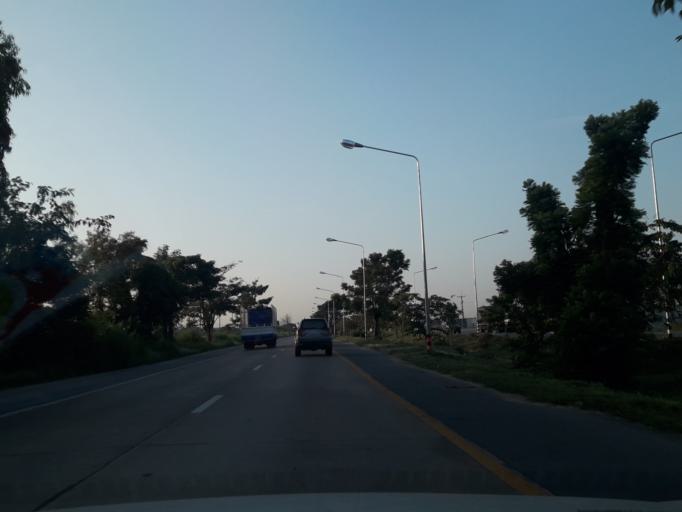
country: TH
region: Phra Nakhon Si Ayutthaya
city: Phra Nakhon Si Ayutthaya
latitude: 14.3267
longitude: 100.5279
